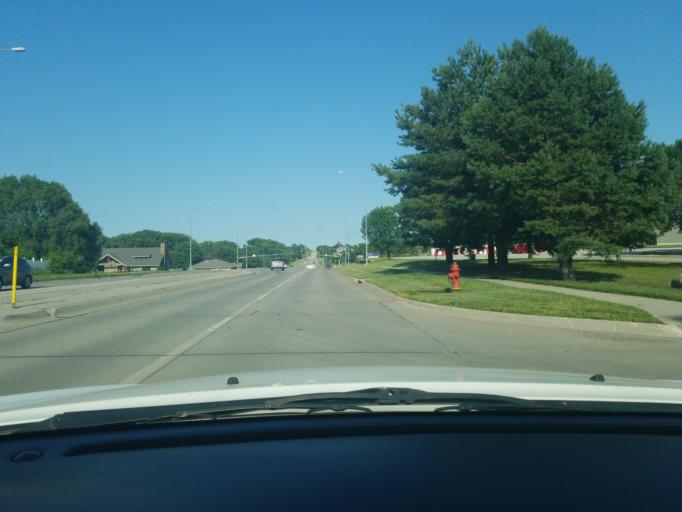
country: US
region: Nebraska
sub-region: Lancaster County
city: Lincoln
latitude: 40.7552
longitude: -96.6088
